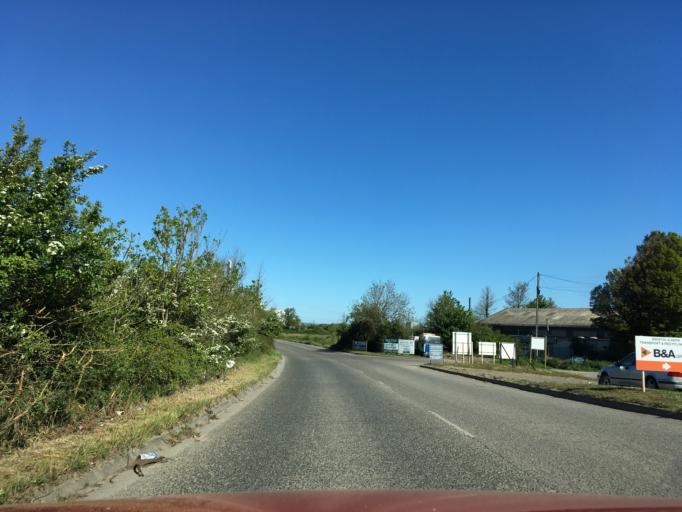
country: GB
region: England
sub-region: South Gloucestershire
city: Severn Beach
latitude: 51.5265
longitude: -2.6586
